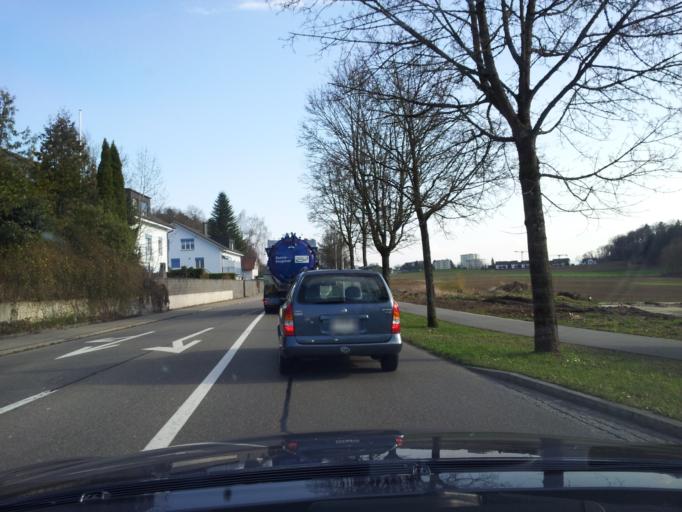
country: CH
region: Aargau
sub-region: Bezirk Baden
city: Niederrohrdorf
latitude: 47.4367
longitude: 8.2989
